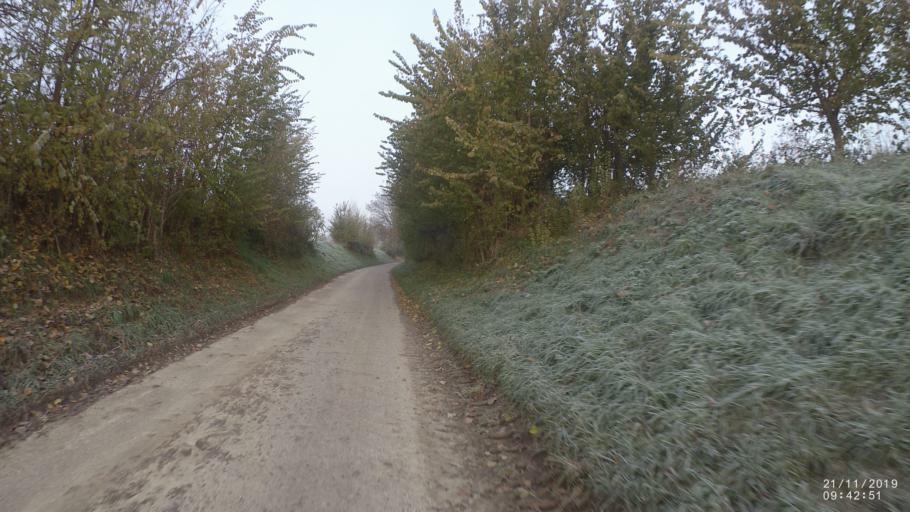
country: BE
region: Flanders
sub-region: Provincie Vlaams-Brabant
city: Tienen
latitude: 50.7827
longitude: 4.9964
